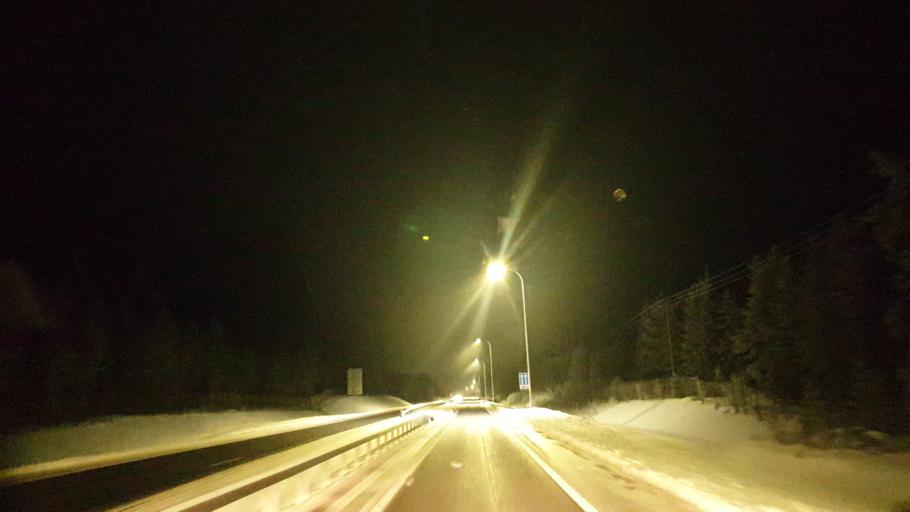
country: FI
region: Northern Ostrobothnia
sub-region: Oulu
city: Haukipudas
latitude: 65.2311
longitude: 25.3914
